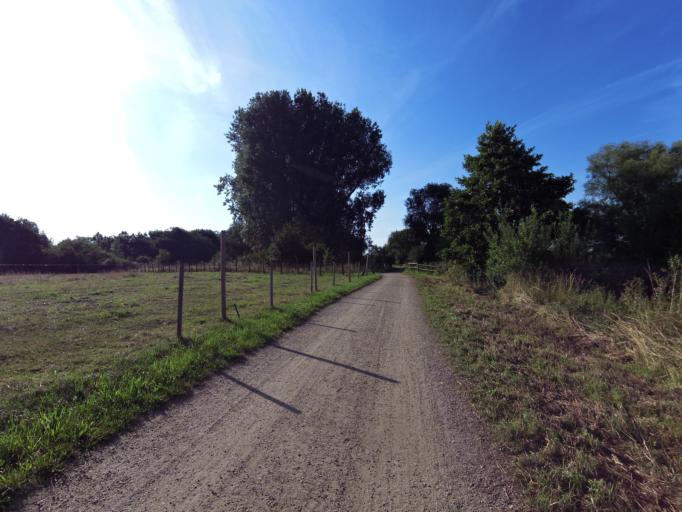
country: DE
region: North Rhine-Westphalia
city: Huckelhoven
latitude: 51.0498
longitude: 6.2055
